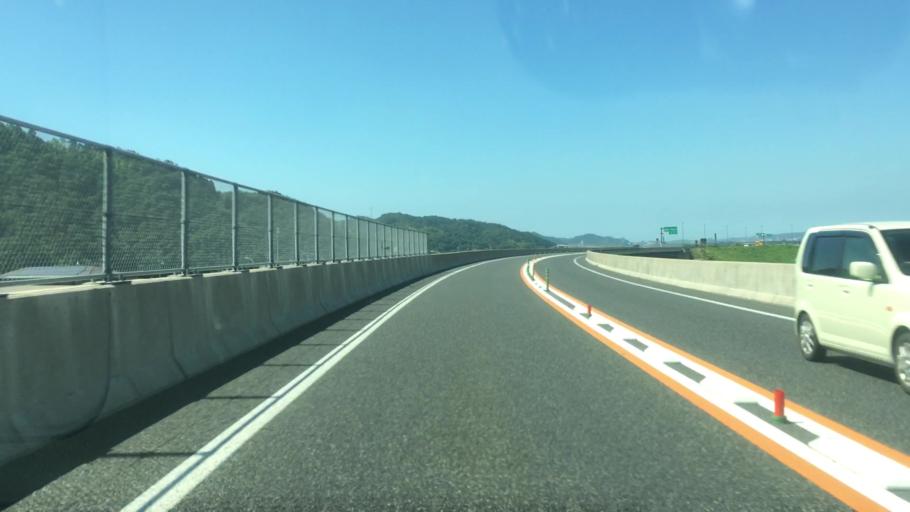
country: JP
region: Tottori
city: Tottori
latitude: 35.4176
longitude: 134.2058
